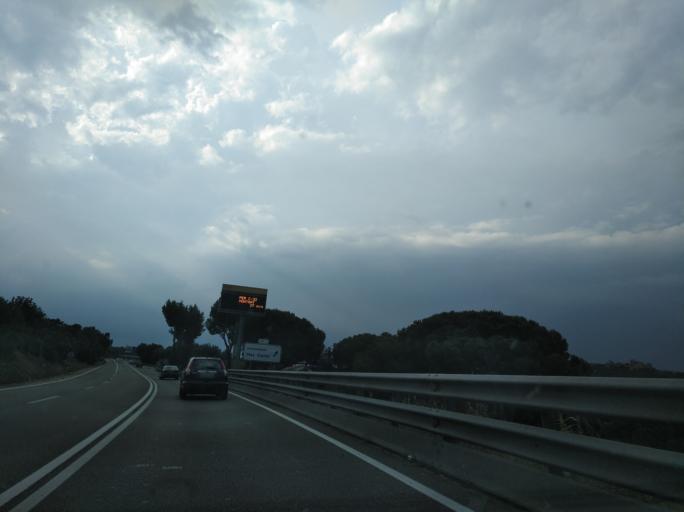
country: ES
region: Catalonia
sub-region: Provincia de Barcelona
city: Palafolls
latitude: 41.6662
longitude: 2.7310
